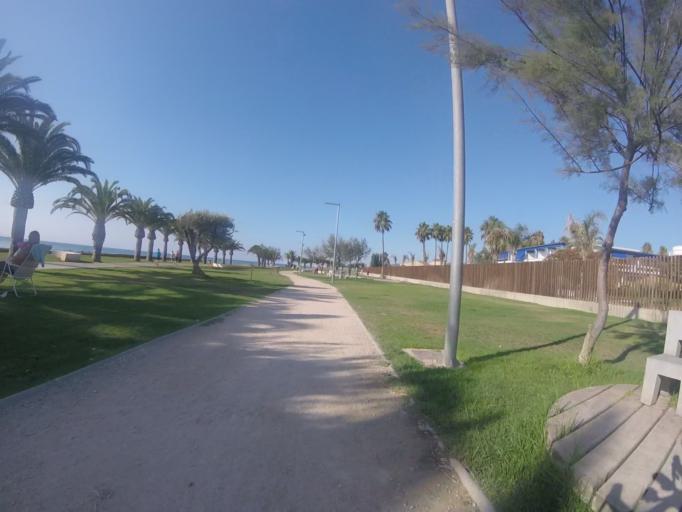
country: ES
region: Valencia
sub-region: Provincia de Castello
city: Benicarlo
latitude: 40.4109
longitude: 0.4295
